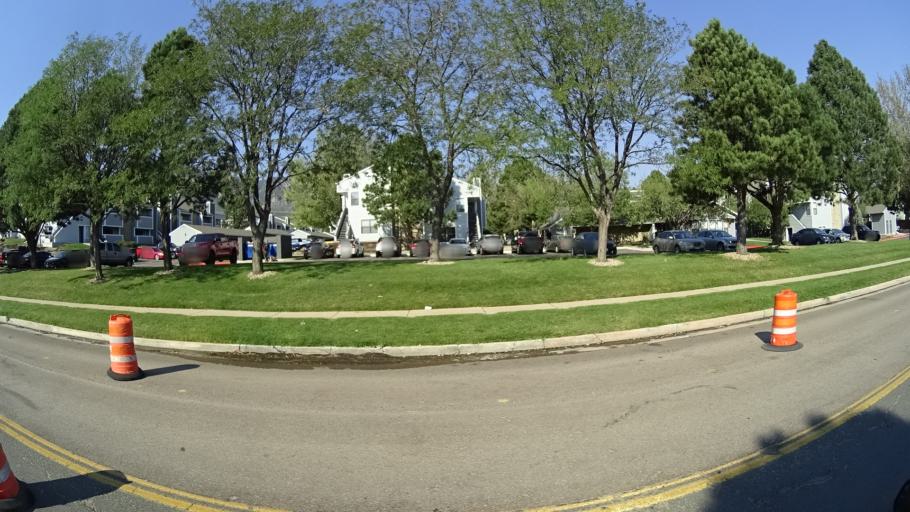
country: US
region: Colorado
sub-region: El Paso County
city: Stratmoor
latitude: 38.7730
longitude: -104.8109
